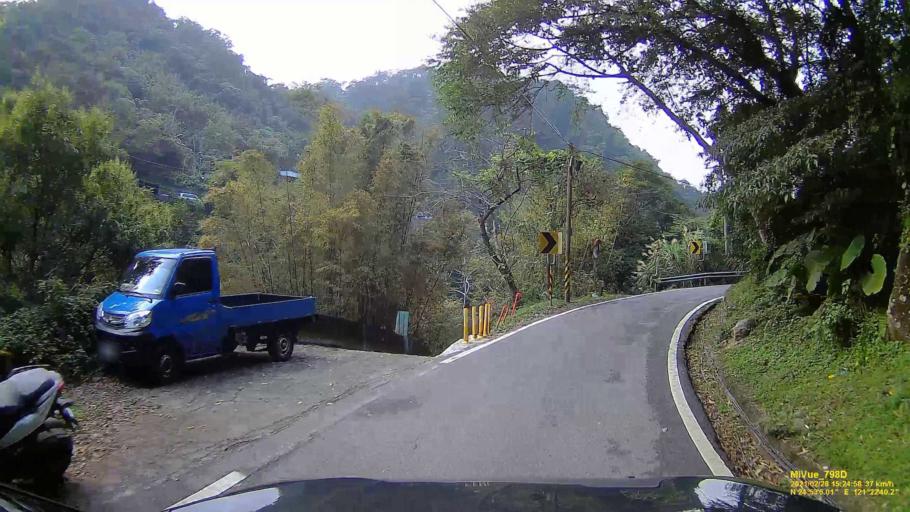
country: TW
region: Taiwan
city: Daxi
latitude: 24.8851
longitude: 121.3777
